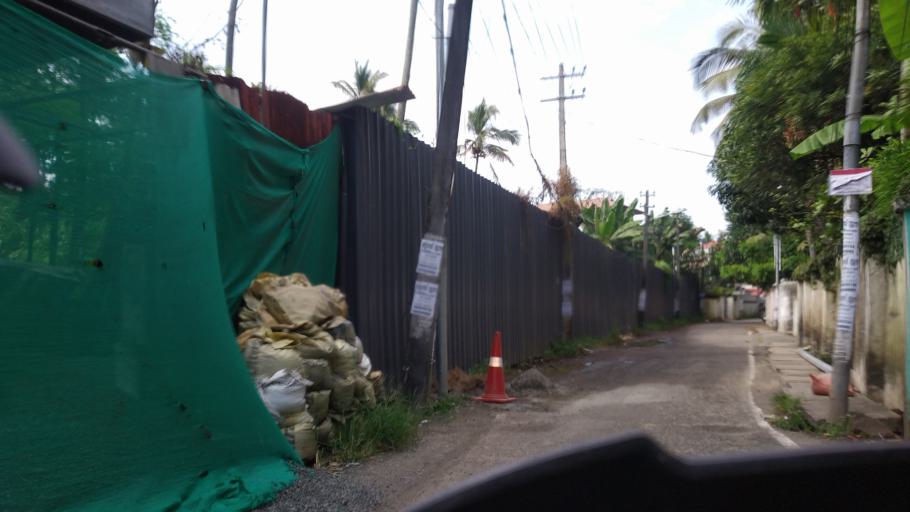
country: IN
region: Kerala
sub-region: Ernakulam
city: Cochin
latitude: 9.9858
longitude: 76.2997
